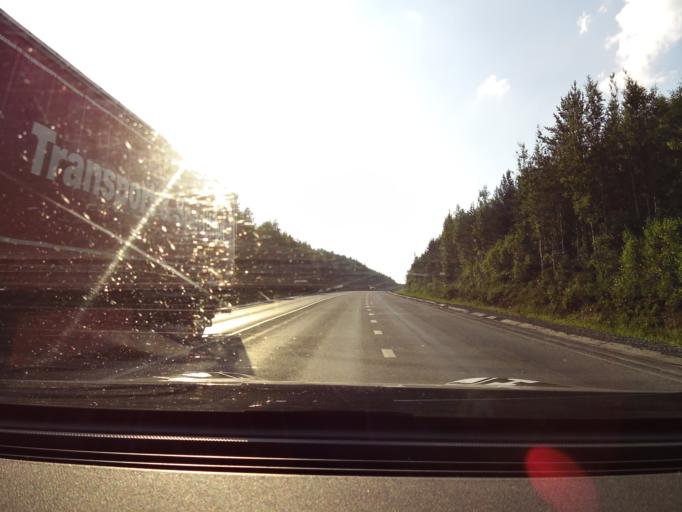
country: RU
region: Sverdlovsk
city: Revda
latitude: 56.8323
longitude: 59.8433
